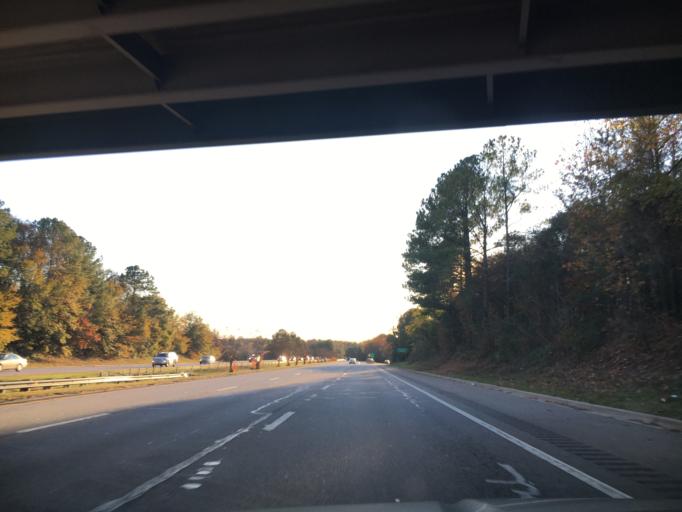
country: US
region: South Carolina
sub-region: Richland County
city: Columbia
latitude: 34.0327
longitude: -81.0315
